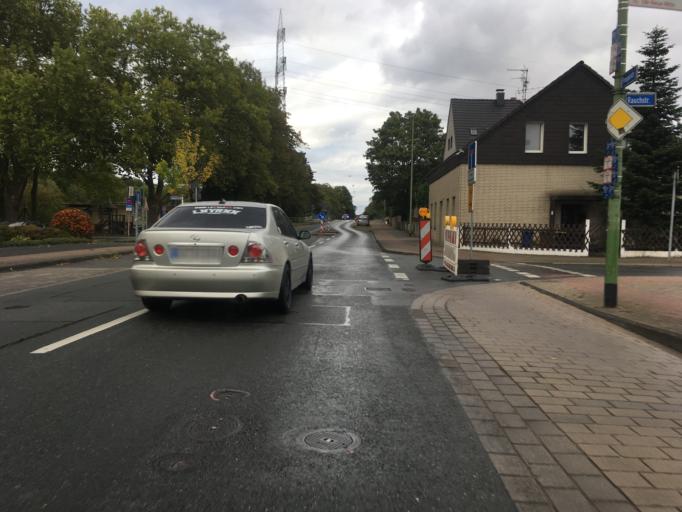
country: DE
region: North Rhine-Westphalia
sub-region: Regierungsbezirk Munster
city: Bottrop
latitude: 51.4962
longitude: 6.9351
